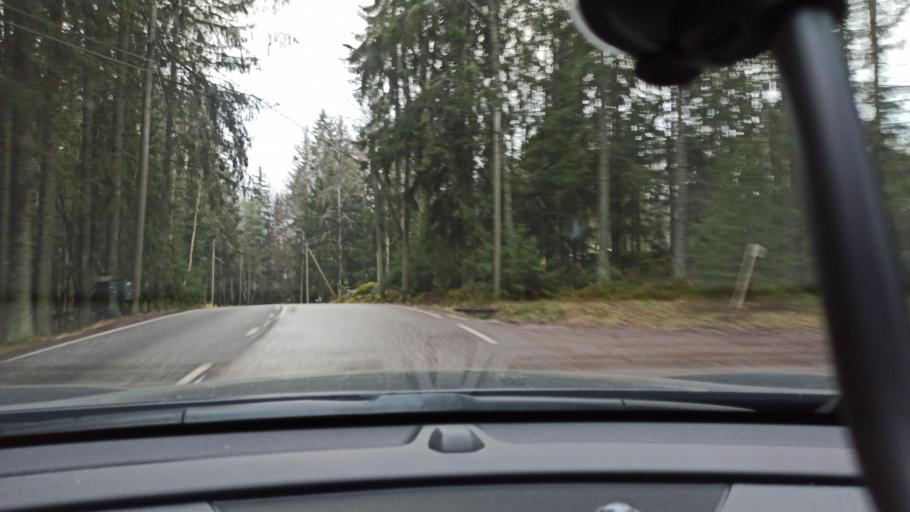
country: FI
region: Uusimaa
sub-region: Helsinki
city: Kirkkonummi
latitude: 60.1481
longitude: 24.4592
